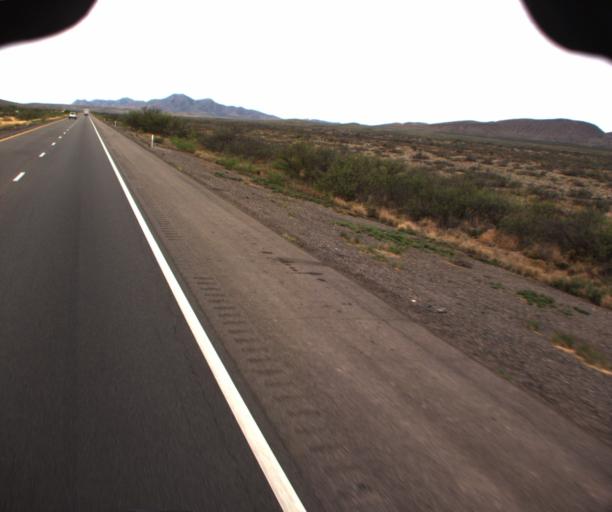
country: US
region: Arizona
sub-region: Cochise County
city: Willcox
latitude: 32.1678
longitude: -109.9643
